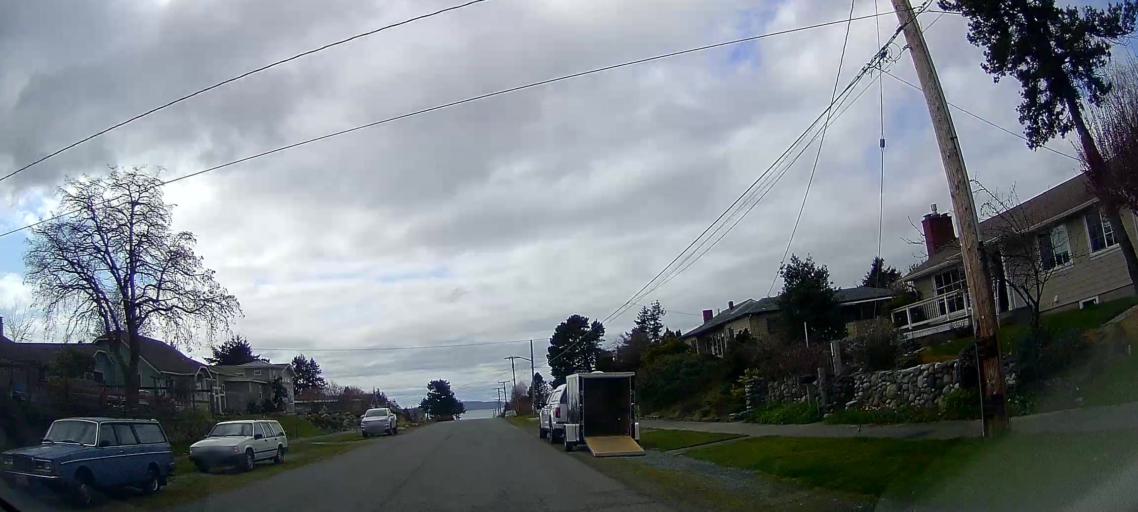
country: US
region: Washington
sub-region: Skagit County
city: Anacortes
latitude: 48.5143
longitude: -122.6271
